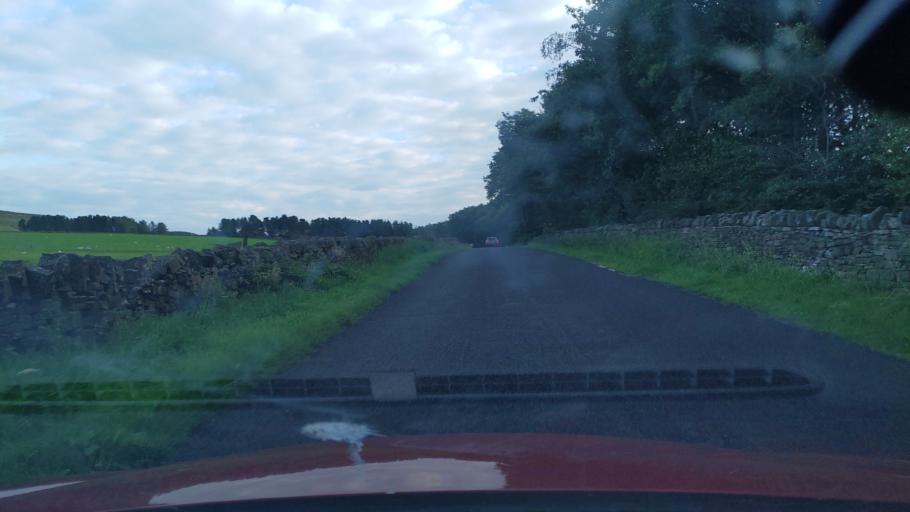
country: GB
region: England
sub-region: Blackburn with Darwen
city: Darwen
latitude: 53.6854
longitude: -2.5093
